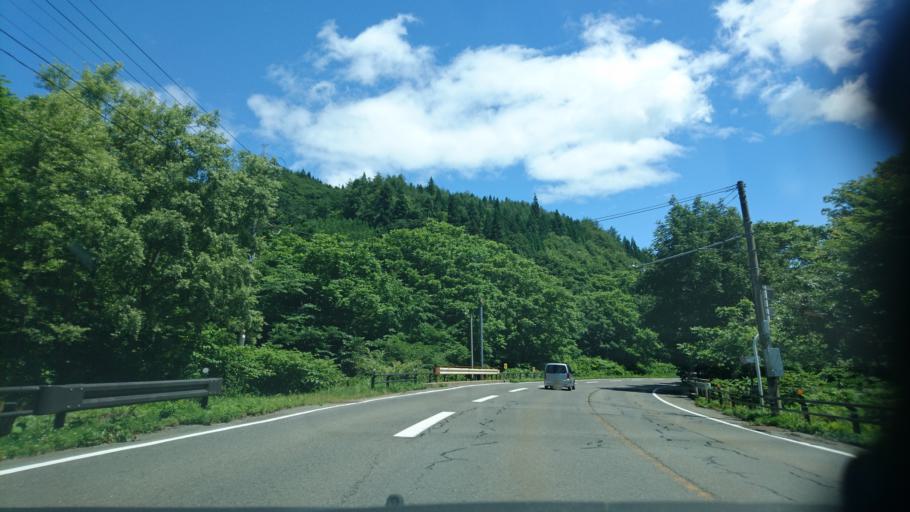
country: JP
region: Akita
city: Kakunodatemachi
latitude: 39.6618
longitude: 140.6756
